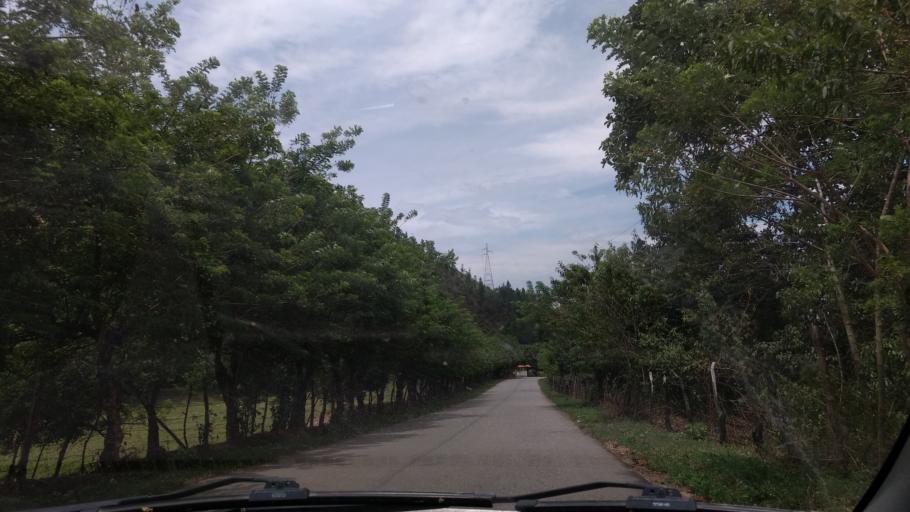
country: CO
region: Cauca
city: Buenos Aires
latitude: 3.0762
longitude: -76.6516
